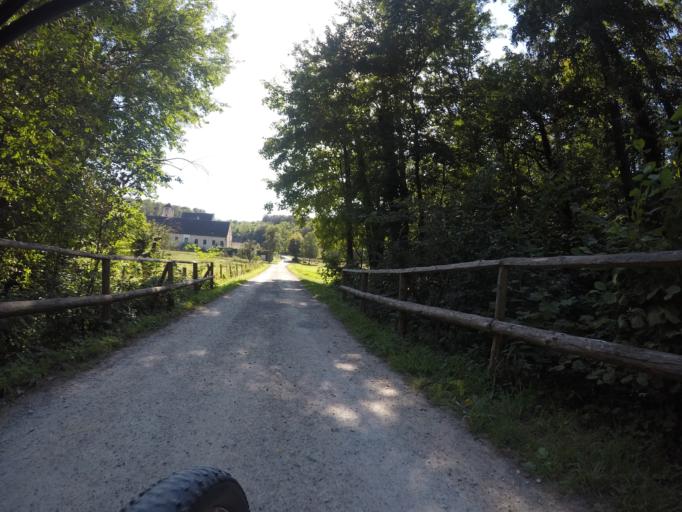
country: AT
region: Lower Austria
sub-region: Politischer Bezirk Bruck an der Leitha
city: Mannersdorf am Leithagebirge
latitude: 47.9549
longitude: 16.6003
